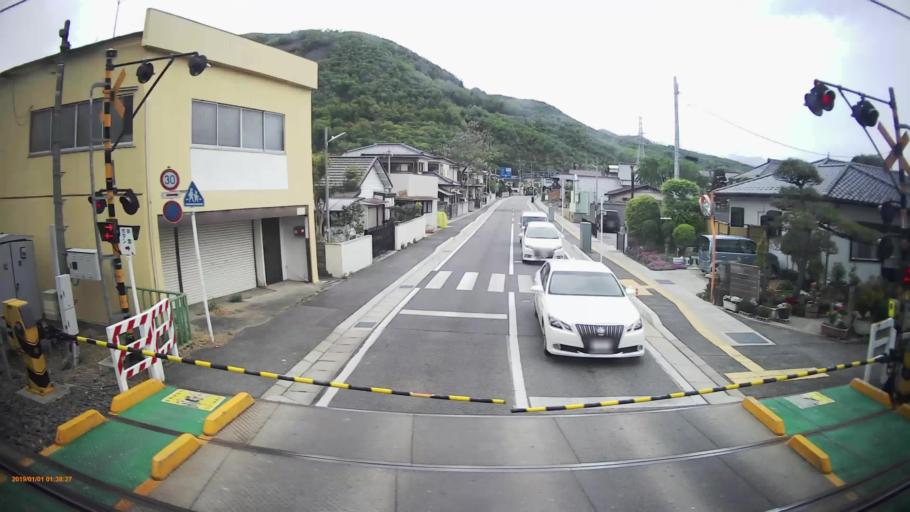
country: JP
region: Yamanashi
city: Isawa
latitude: 35.6579
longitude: 138.6380
